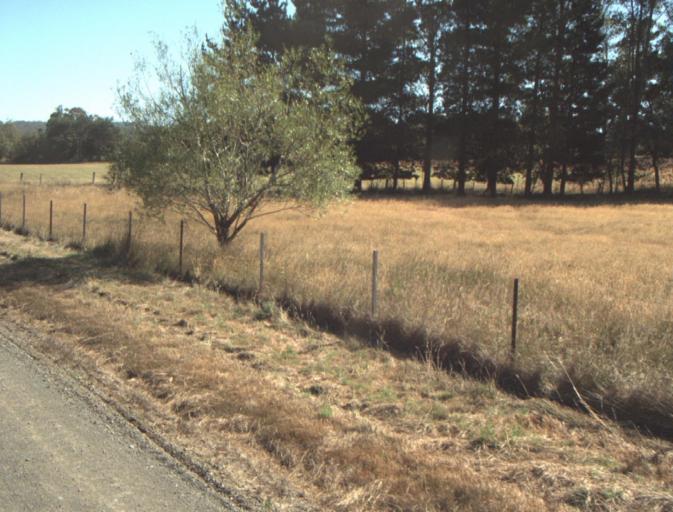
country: AU
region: Tasmania
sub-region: Launceston
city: Newstead
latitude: -41.3215
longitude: 147.3206
